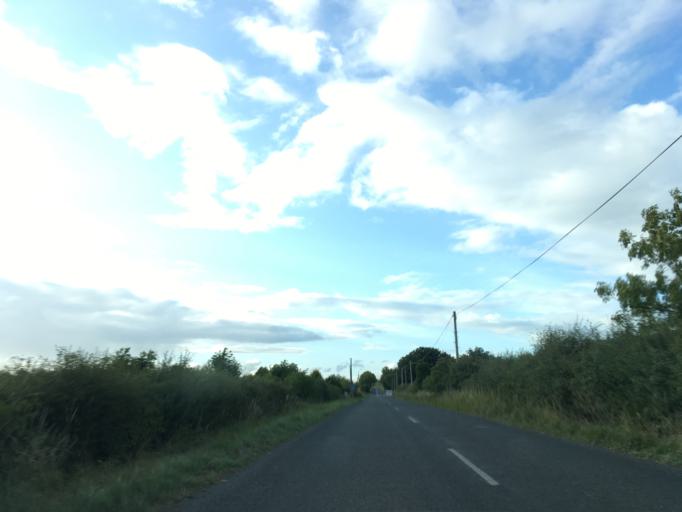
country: IE
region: Munster
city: Cashel
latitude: 52.4637
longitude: -7.9181
